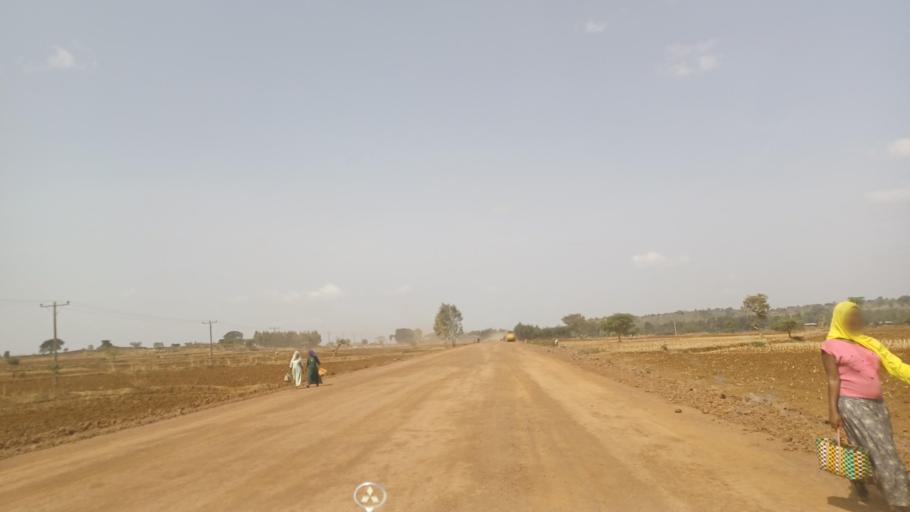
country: ET
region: Amhara
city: Bahir Dar
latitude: 11.8582
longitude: 37.0124
